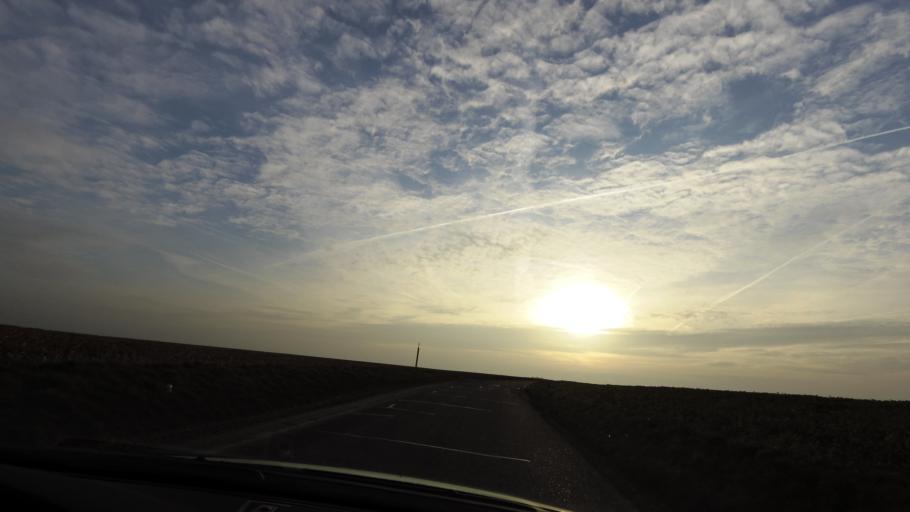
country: NL
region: Limburg
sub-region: Gemeente Nuth
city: Nuth
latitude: 50.9195
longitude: 5.8437
